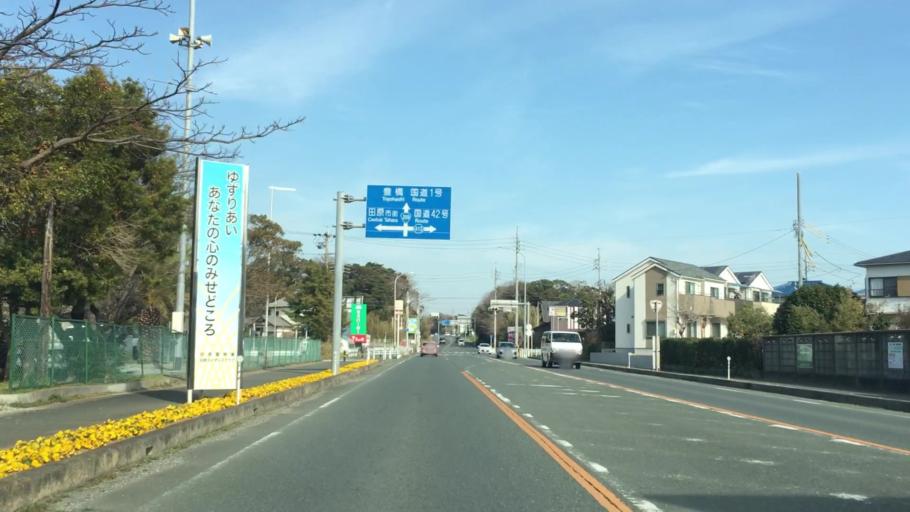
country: JP
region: Aichi
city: Tahara
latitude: 34.6627
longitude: 137.2758
